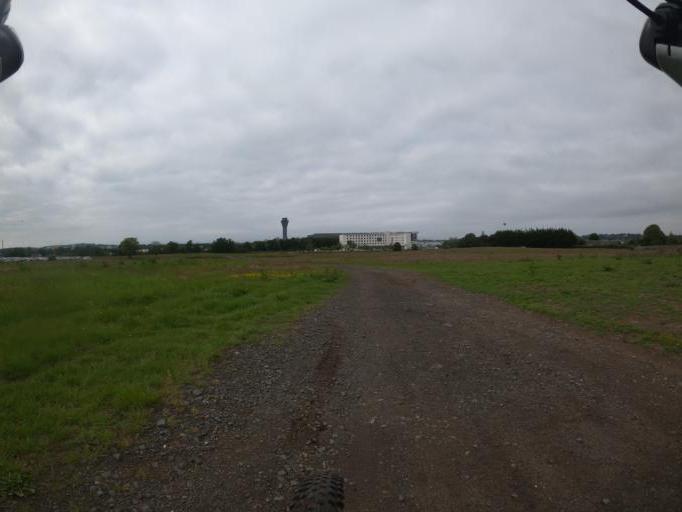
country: GB
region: Scotland
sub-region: Edinburgh
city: Ratho
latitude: 55.9408
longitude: -3.3632
